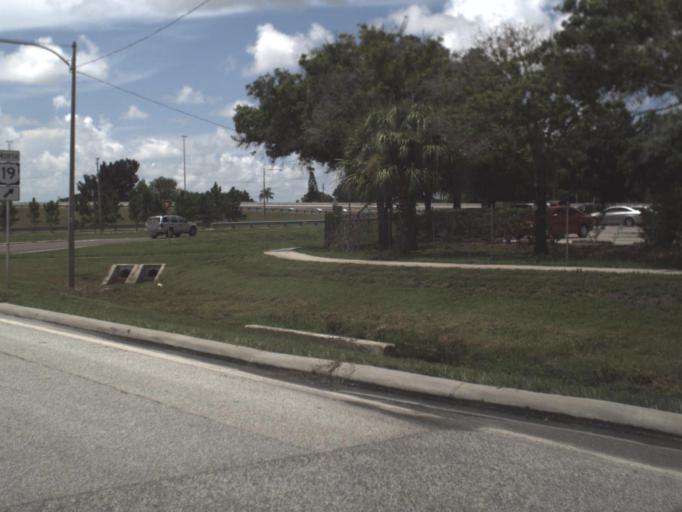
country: US
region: Florida
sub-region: Pinellas County
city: Pinellas Park
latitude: 27.8657
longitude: -82.7003
